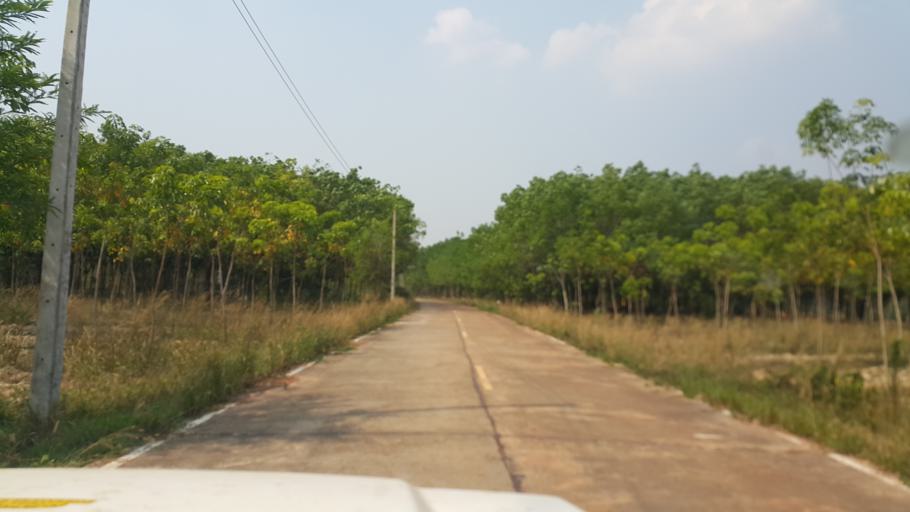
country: TH
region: Nakhon Phanom
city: Ban Phaeng
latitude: 17.9662
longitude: 104.1543
